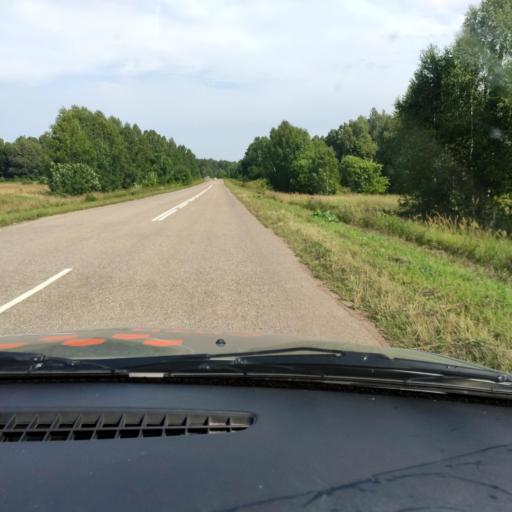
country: RU
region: Bashkortostan
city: Pavlovka
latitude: 55.3856
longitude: 56.4950
